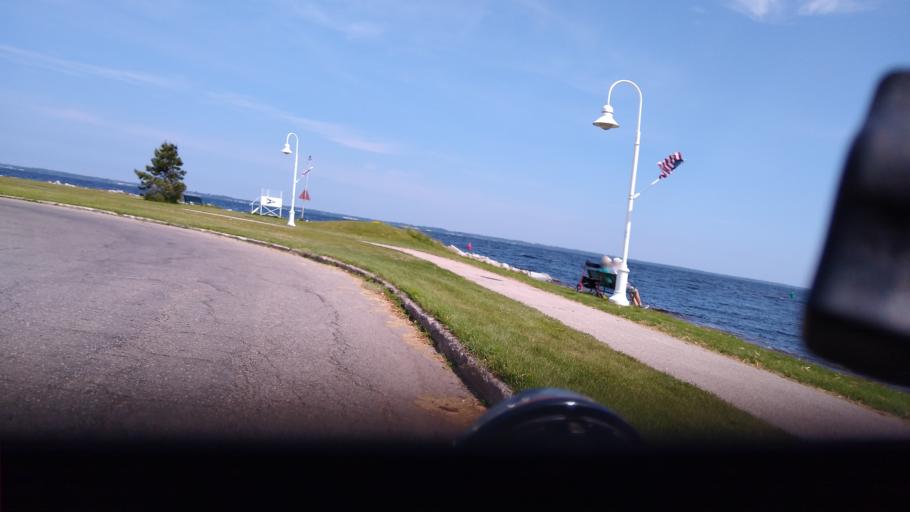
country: US
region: Michigan
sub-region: Delta County
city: Escanaba
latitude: 45.7431
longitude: -87.0385
